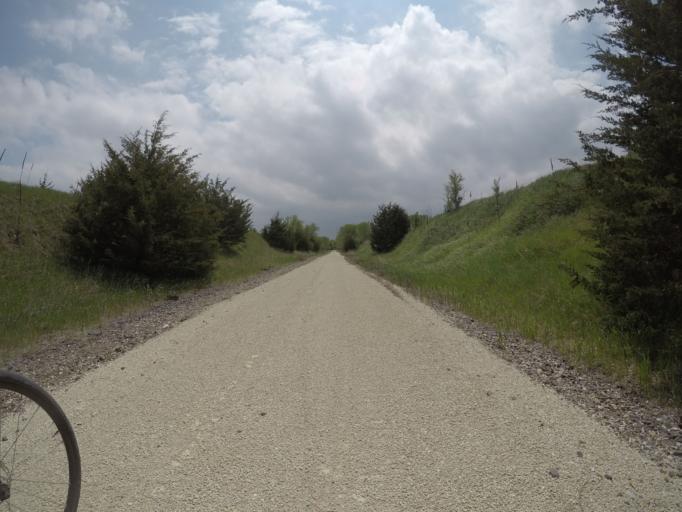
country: US
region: Nebraska
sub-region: Gage County
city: Wymore
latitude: 40.2060
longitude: -96.6608
